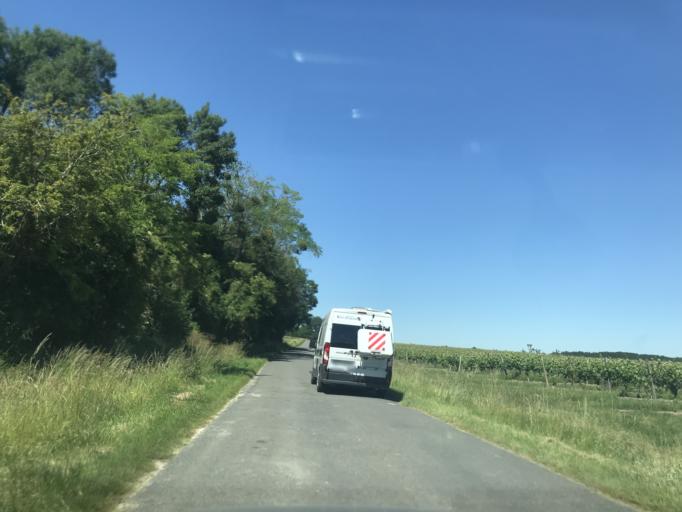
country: FR
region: Poitou-Charentes
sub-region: Departement de la Charente-Maritime
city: Mortagne-sur-Gironde
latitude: 45.4224
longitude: -0.7124
